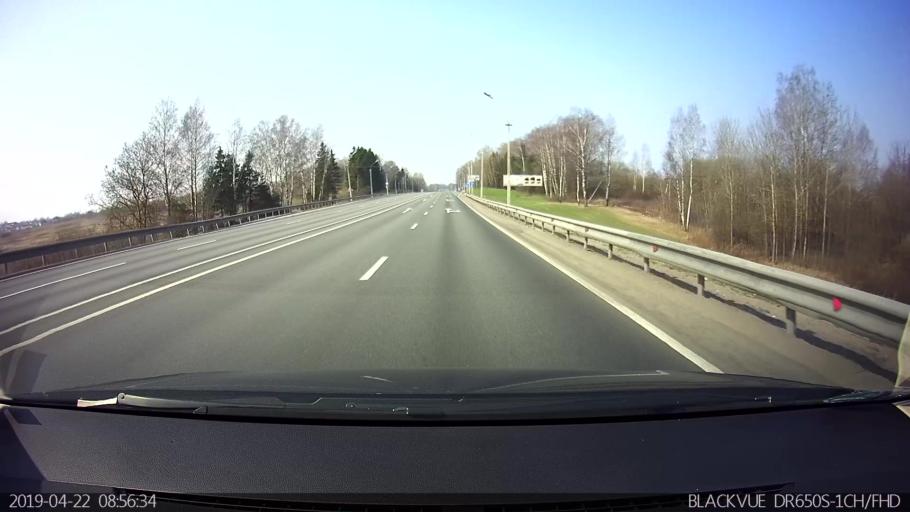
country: RU
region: Smolensk
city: Pechersk
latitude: 54.8736
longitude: 32.0351
